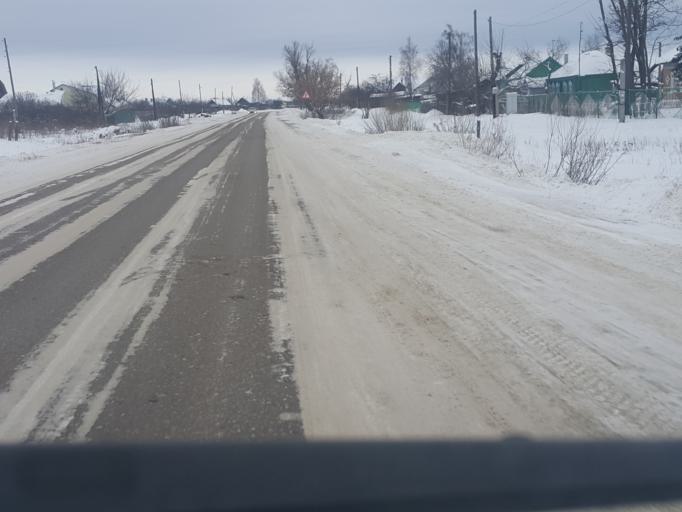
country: RU
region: Tambov
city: Platonovka
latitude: 52.8406
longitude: 41.8126
